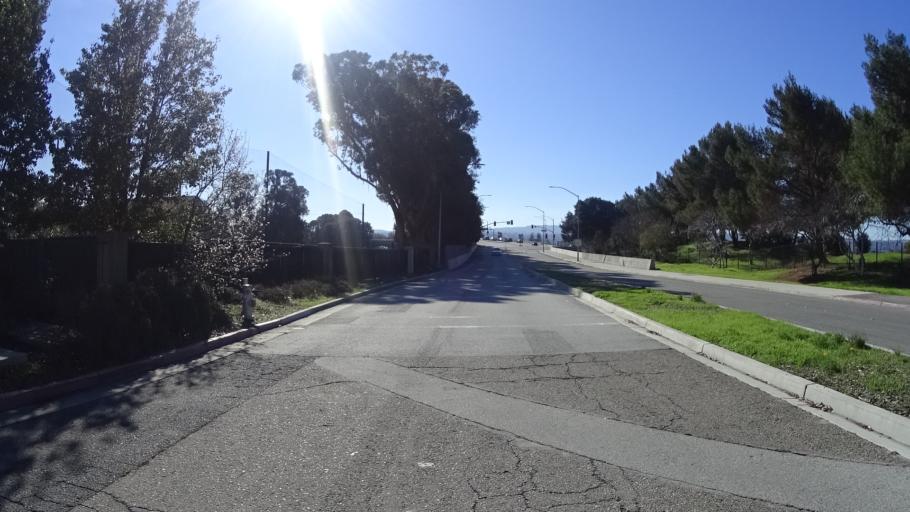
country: US
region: California
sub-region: San Mateo County
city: San Mateo
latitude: 37.5862
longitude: -122.3261
